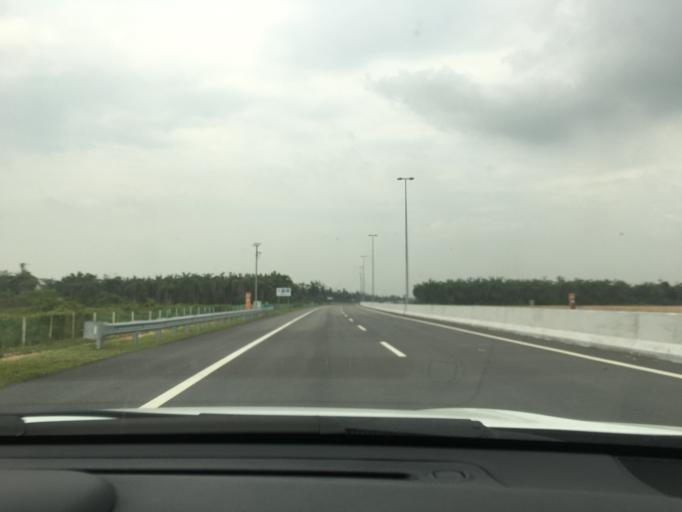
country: MY
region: Selangor
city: Klang
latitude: 3.0995
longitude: 101.4249
